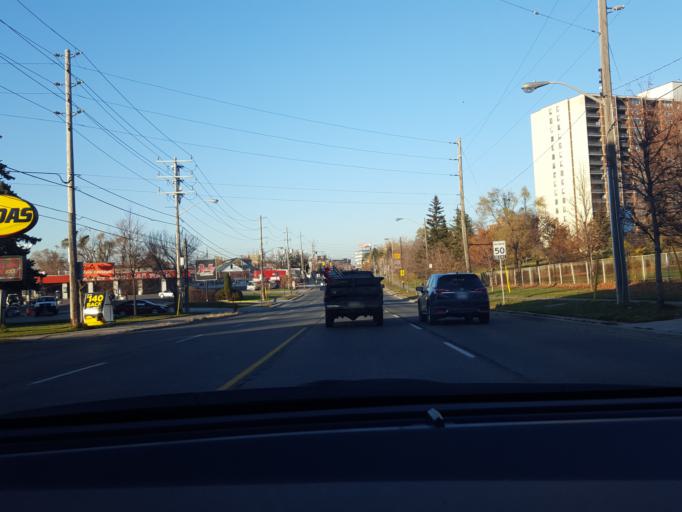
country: CA
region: Ontario
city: Scarborough
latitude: 43.7167
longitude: -79.3047
